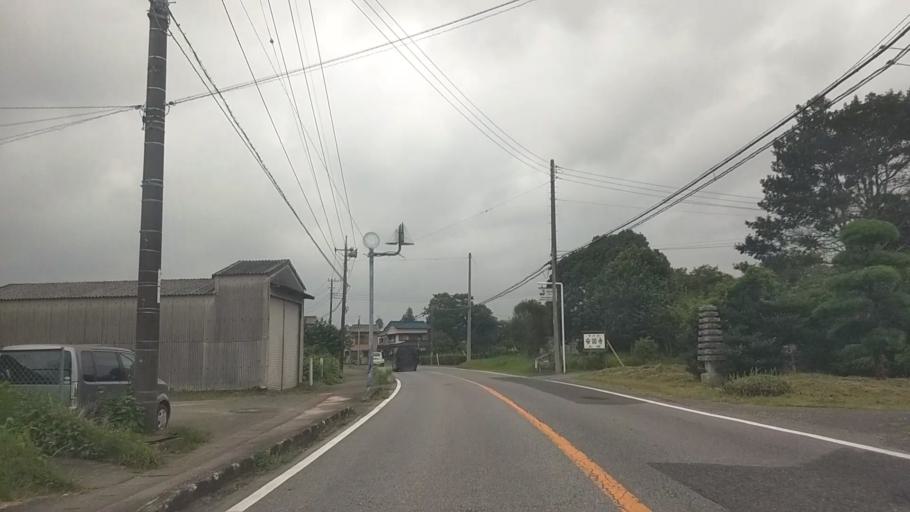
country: JP
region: Chiba
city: Kawaguchi
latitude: 35.1352
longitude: 140.0026
